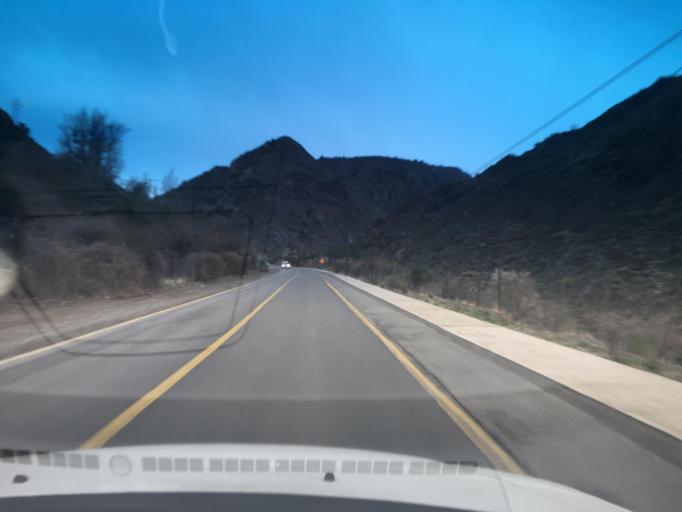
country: CL
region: Santiago Metropolitan
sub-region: Provincia de Cordillera
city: Puente Alto
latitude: -33.7380
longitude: -70.2988
